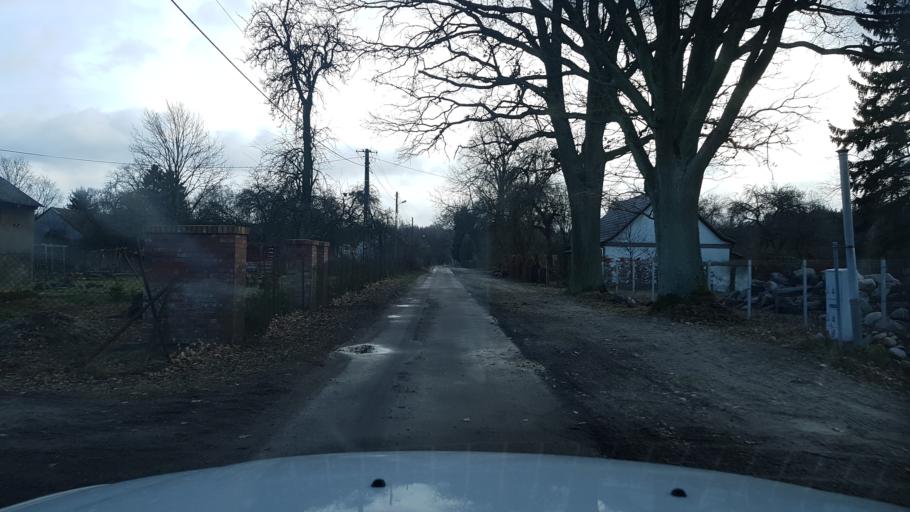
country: PL
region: West Pomeranian Voivodeship
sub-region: Powiat szczecinecki
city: Borne Sulinowo
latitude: 53.6189
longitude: 16.6156
